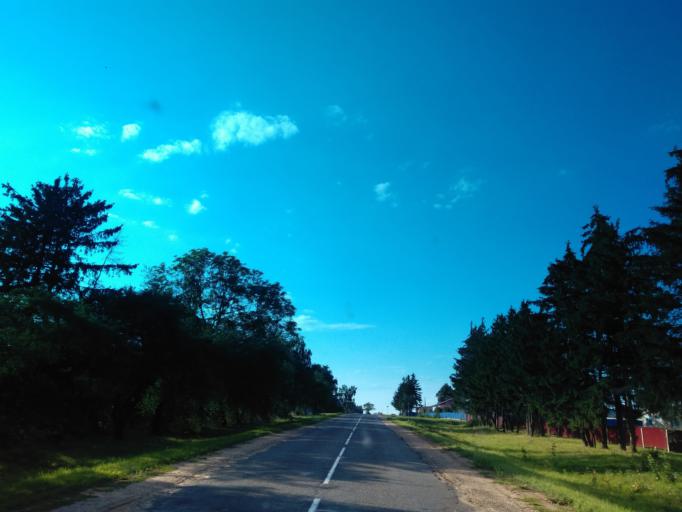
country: BY
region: Minsk
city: Kapyl'
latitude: 53.1735
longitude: 27.0764
